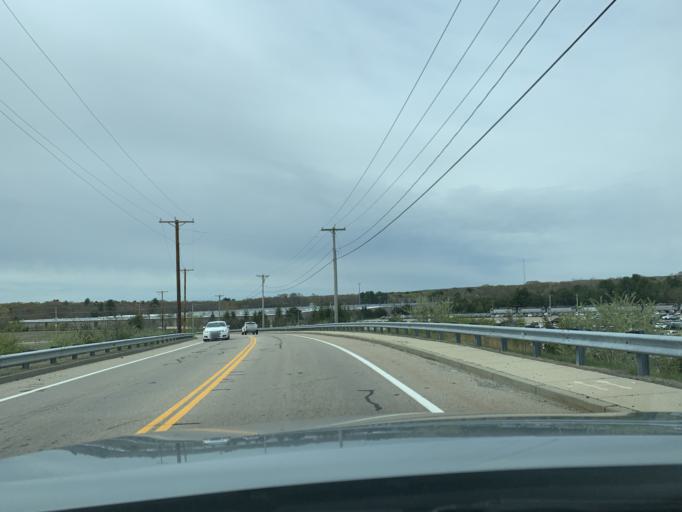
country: US
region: Rhode Island
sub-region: Kent County
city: East Greenwich
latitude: 41.6078
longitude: -71.4728
